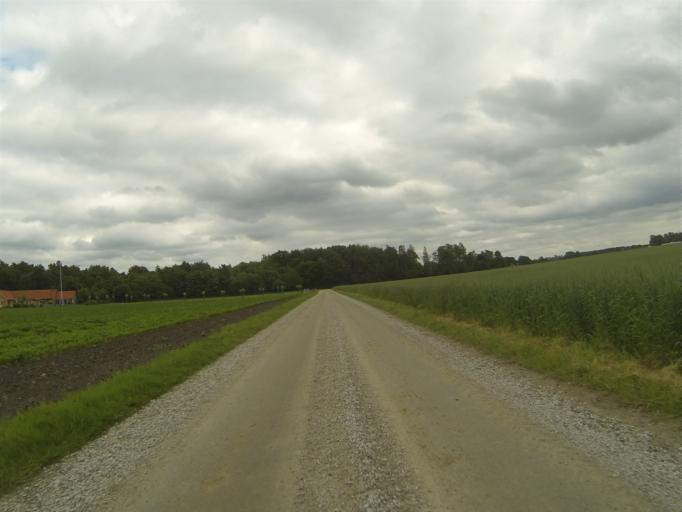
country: SE
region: Skane
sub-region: Lunds Kommun
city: Lund
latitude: 55.7274
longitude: 13.2880
